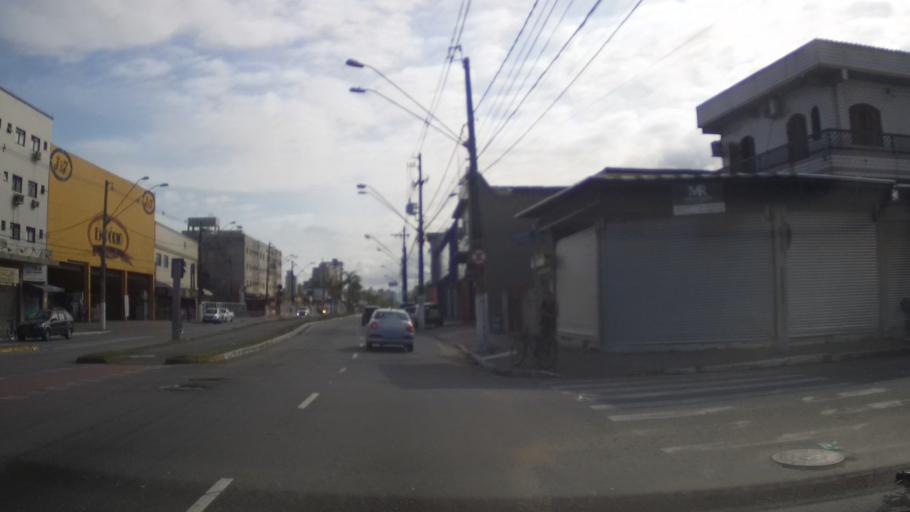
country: BR
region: Sao Paulo
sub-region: Praia Grande
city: Praia Grande
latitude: -24.0145
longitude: -46.4489
